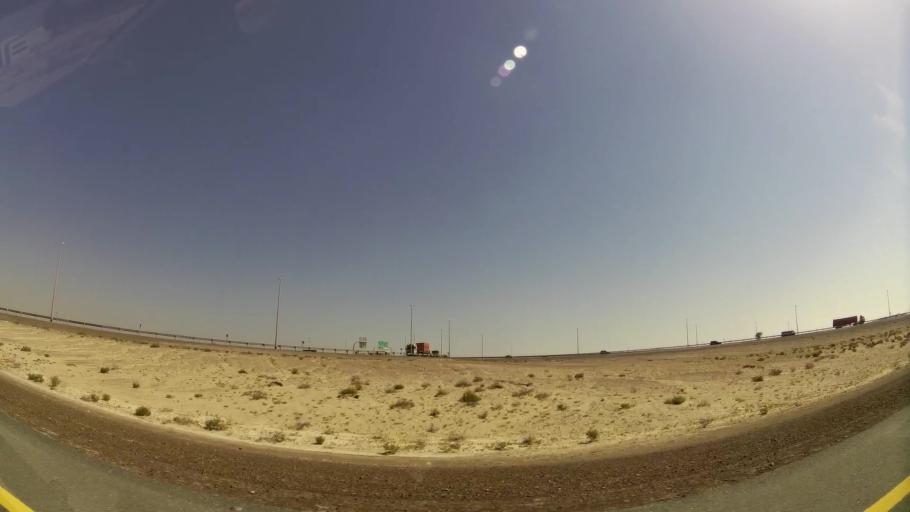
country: AE
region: Dubai
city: Dubai
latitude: 24.9437
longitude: 55.0635
